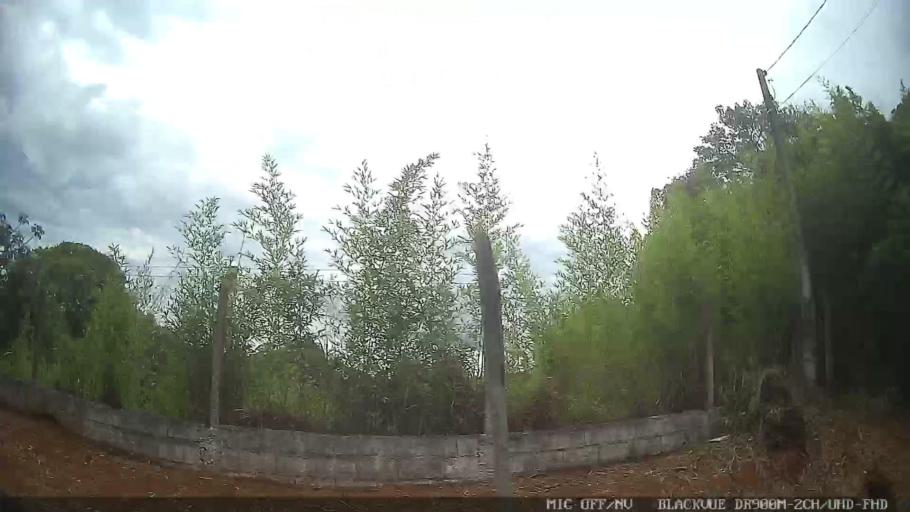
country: BR
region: Sao Paulo
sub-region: Suzano
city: Suzano
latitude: -23.6278
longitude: -46.2862
